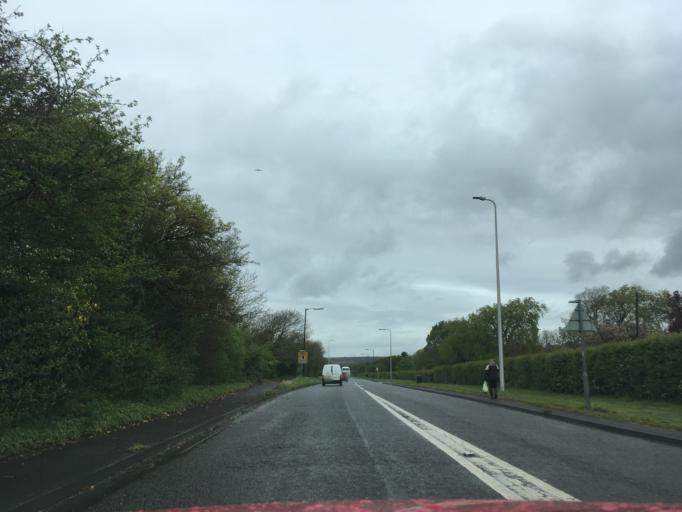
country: GB
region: England
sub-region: North Somerset
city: Banwell
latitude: 51.3319
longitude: -2.8990
